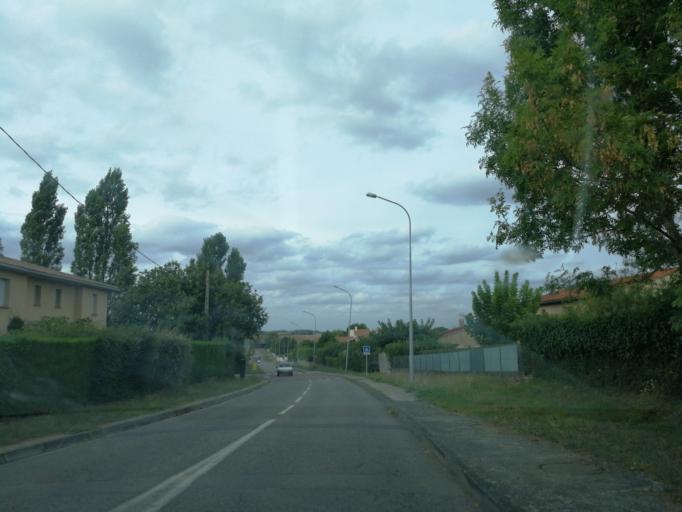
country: FR
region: Midi-Pyrenees
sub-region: Departement de la Haute-Garonne
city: Dremil-Lafage
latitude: 43.5995
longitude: 1.6046
